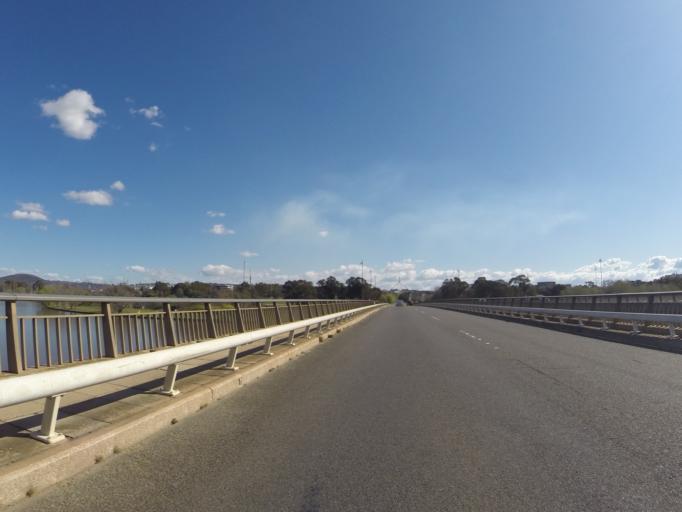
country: AU
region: Australian Capital Territory
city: Forrest
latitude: -35.3015
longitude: 149.1418
